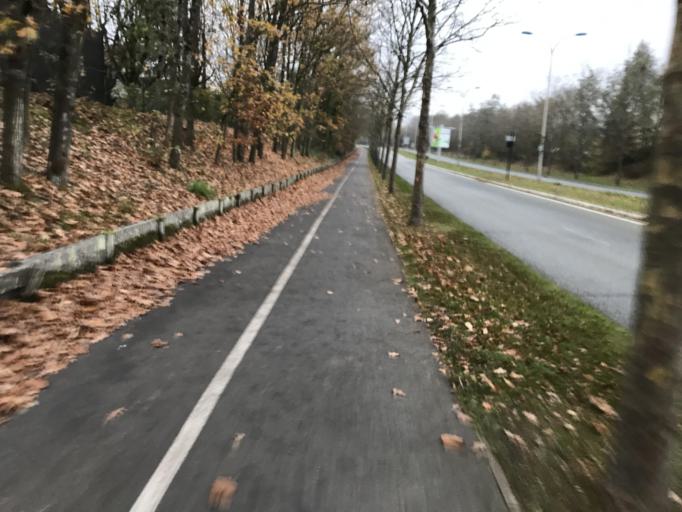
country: FR
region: Ile-de-France
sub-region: Departement des Yvelines
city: Saint-Quentin-en-Yvelines
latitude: 48.7660
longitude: 2.0120
